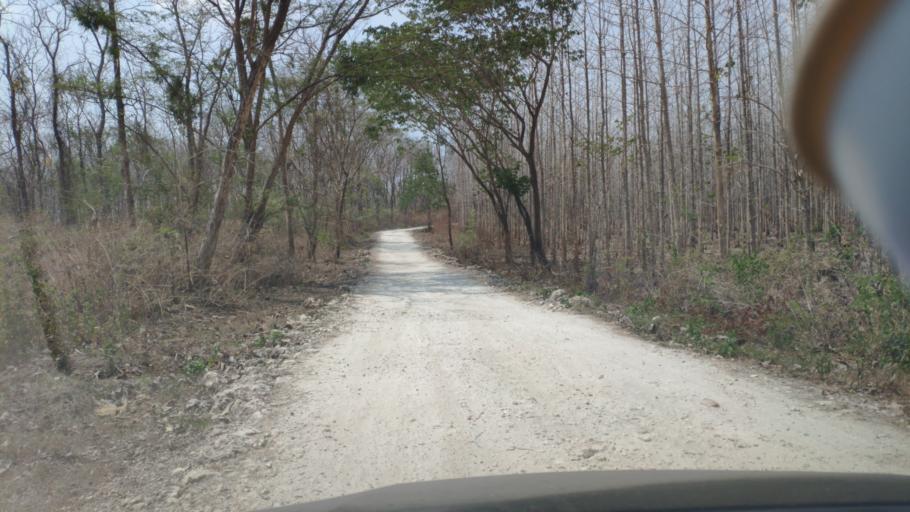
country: ID
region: Central Java
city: Pipes
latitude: -7.1424
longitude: 111.2634
